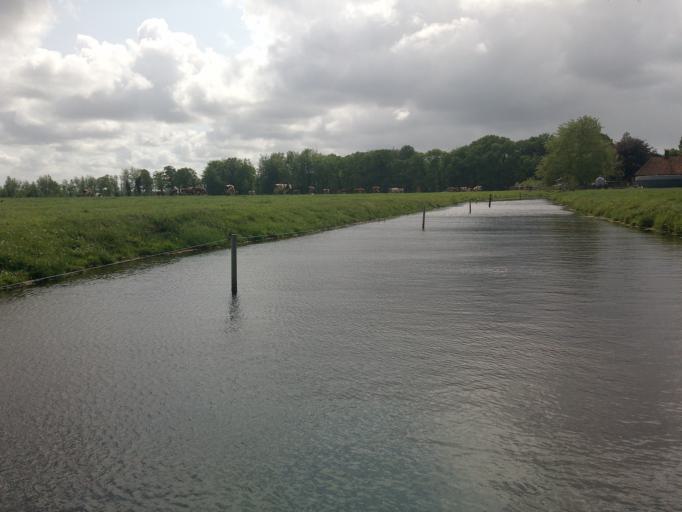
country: NL
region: South Holland
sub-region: Gemeente Wassenaar
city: Wassenaar
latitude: 52.1273
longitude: 4.4027
